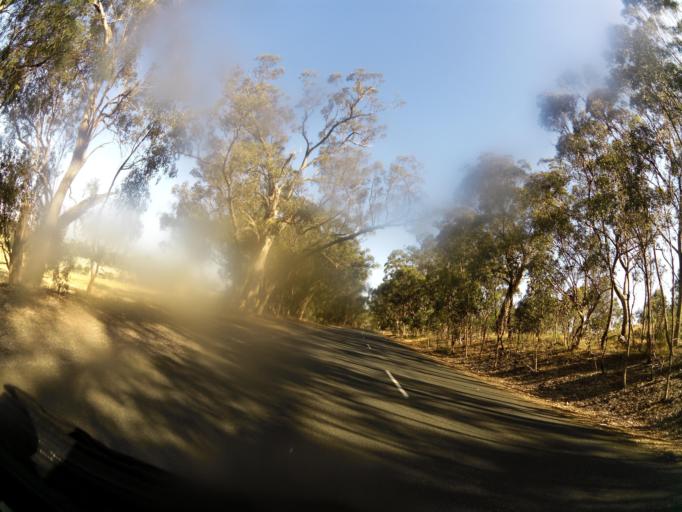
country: AU
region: Victoria
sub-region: Murrindindi
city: Kinglake West
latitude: -37.0050
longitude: 145.1218
